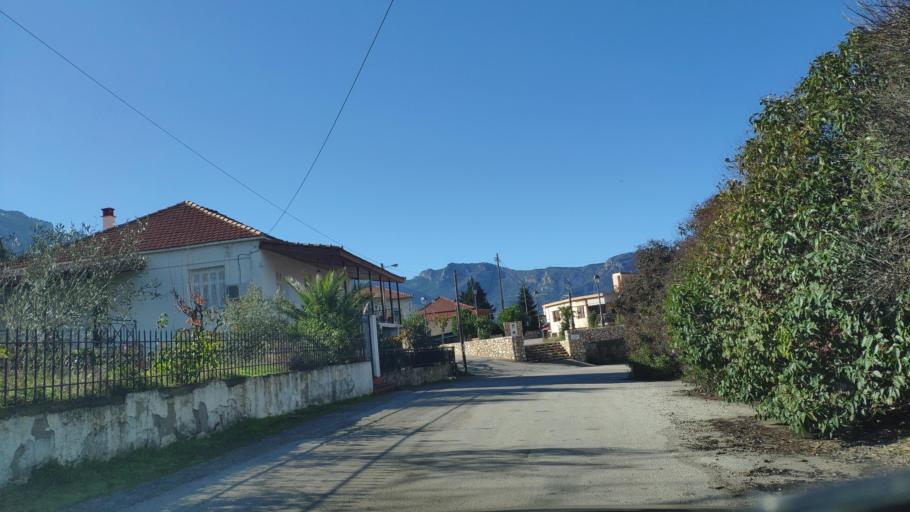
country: GR
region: West Greece
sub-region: Nomos Achaias
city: Aiyira
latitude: 38.0880
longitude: 22.4390
